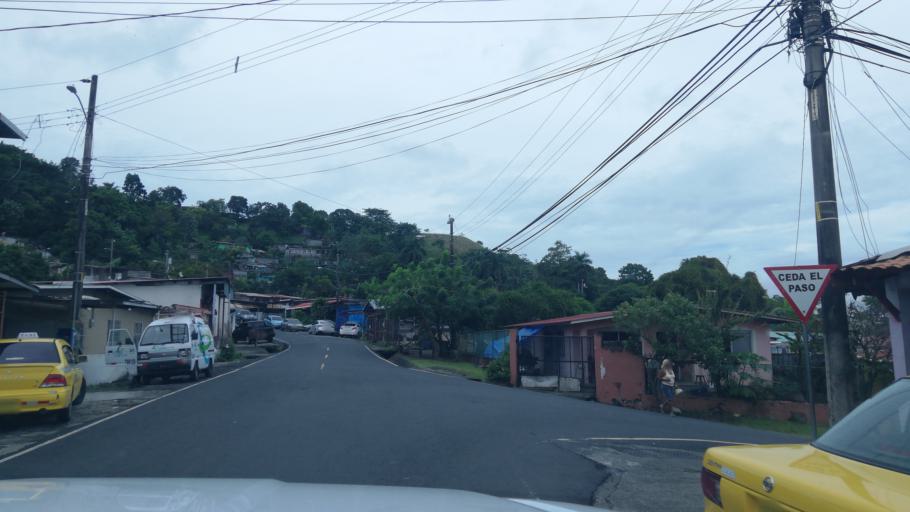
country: PA
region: Panama
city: Las Cumbres
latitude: 9.0718
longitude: -79.5141
